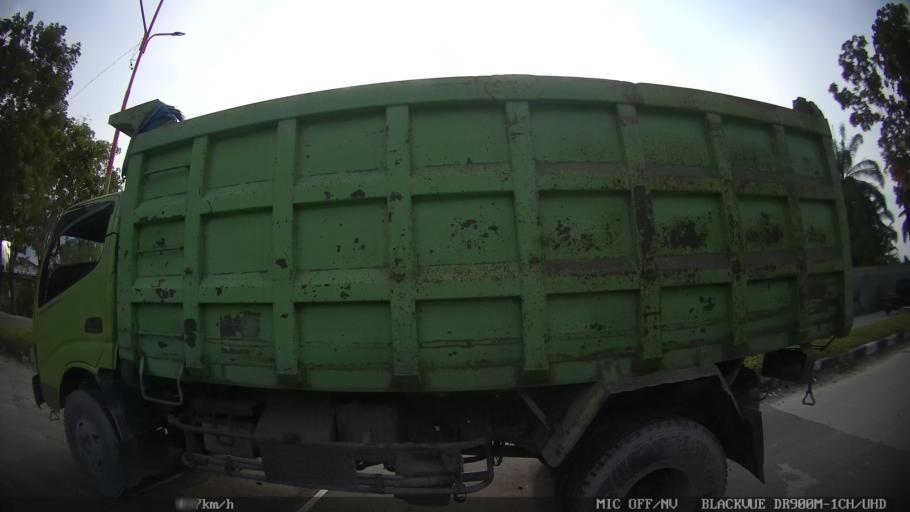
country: ID
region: North Sumatra
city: Binjai
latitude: 3.6092
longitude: 98.5342
